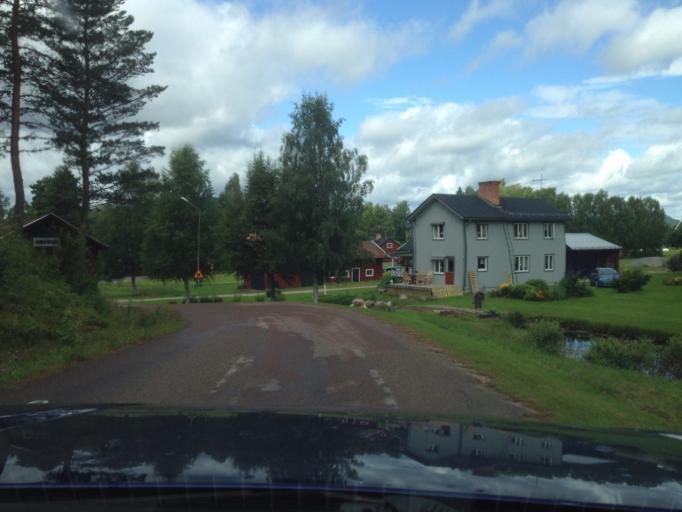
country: SE
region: Dalarna
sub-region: Vansbro Kommun
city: Jarna
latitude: 60.3280
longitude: 14.5366
